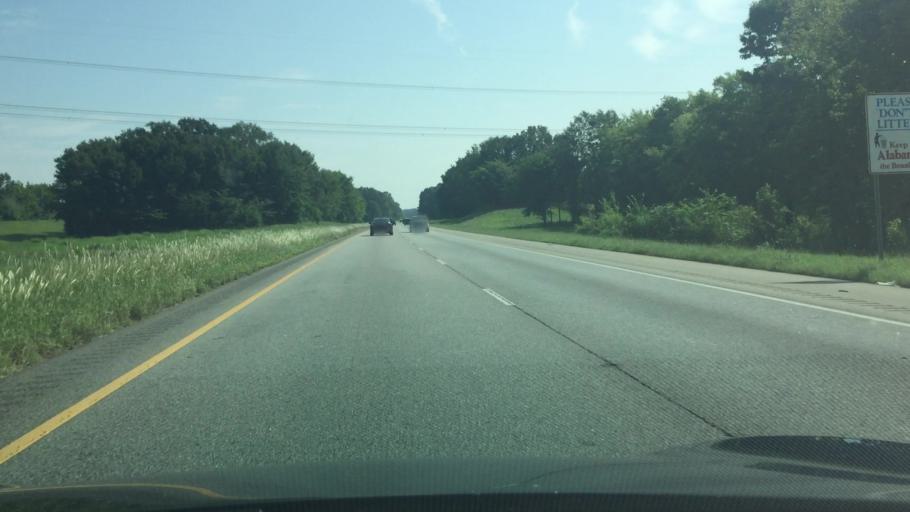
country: US
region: Alabama
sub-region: Lowndes County
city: Hayneville
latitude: 32.2133
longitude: -86.4041
